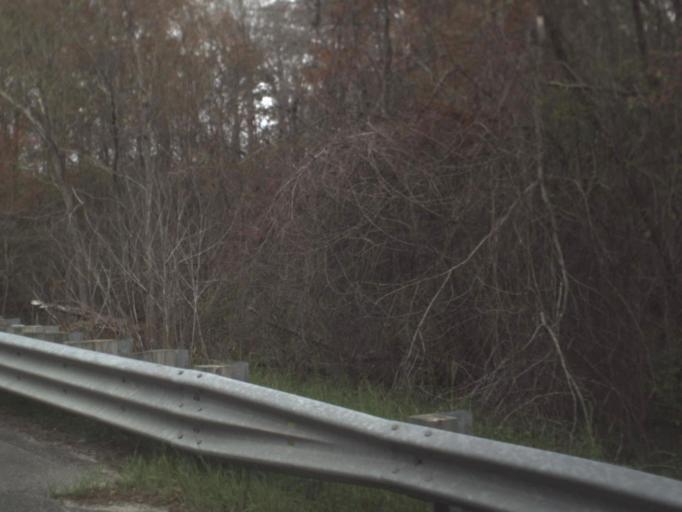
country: US
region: Florida
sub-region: Jefferson County
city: Monticello
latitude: 30.5316
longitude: -83.8122
